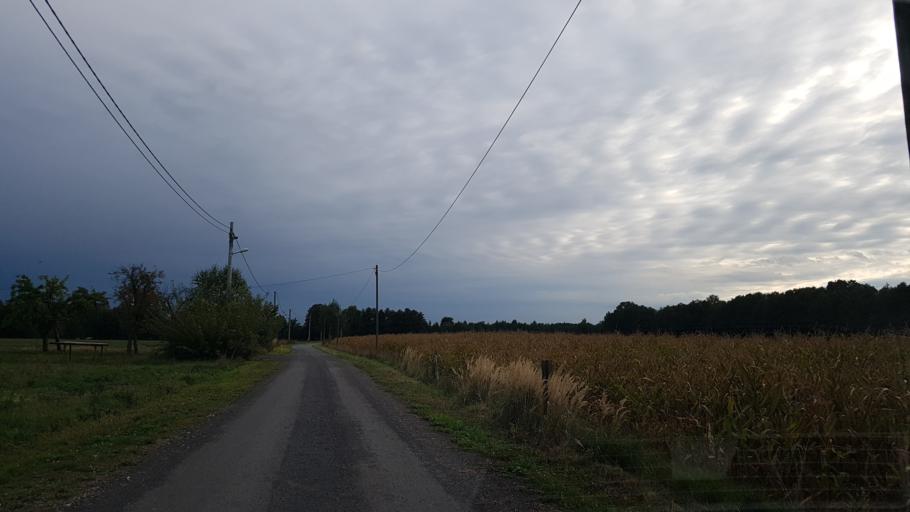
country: DE
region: Brandenburg
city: Bad Liebenwerda
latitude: 51.5306
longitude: 13.4389
